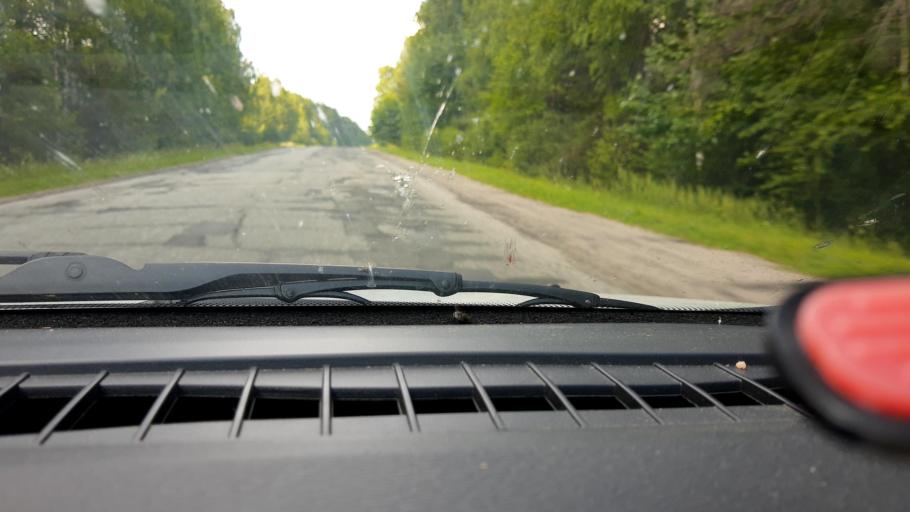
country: RU
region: Nizjnij Novgorod
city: Prudy
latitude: 57.4109
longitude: 46.0731
